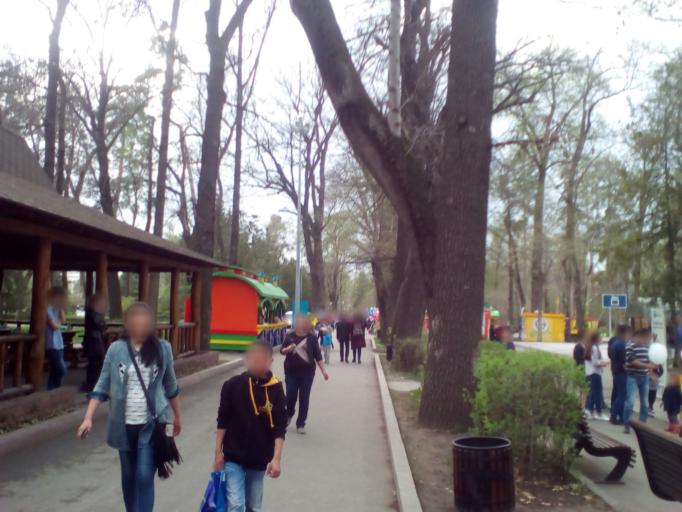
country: KZ
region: Almaty Qalasy
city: Almaty
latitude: 43.2620
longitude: 76.9695
